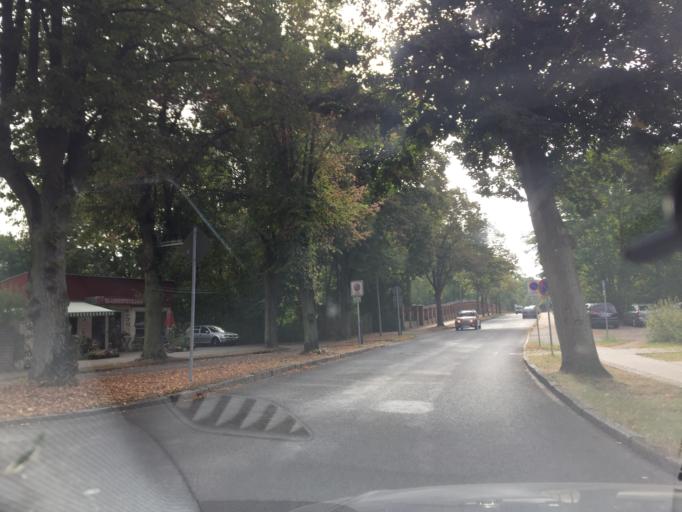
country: DE
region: Brandenburg
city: Erkner
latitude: 52.4187
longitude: 13.7578
